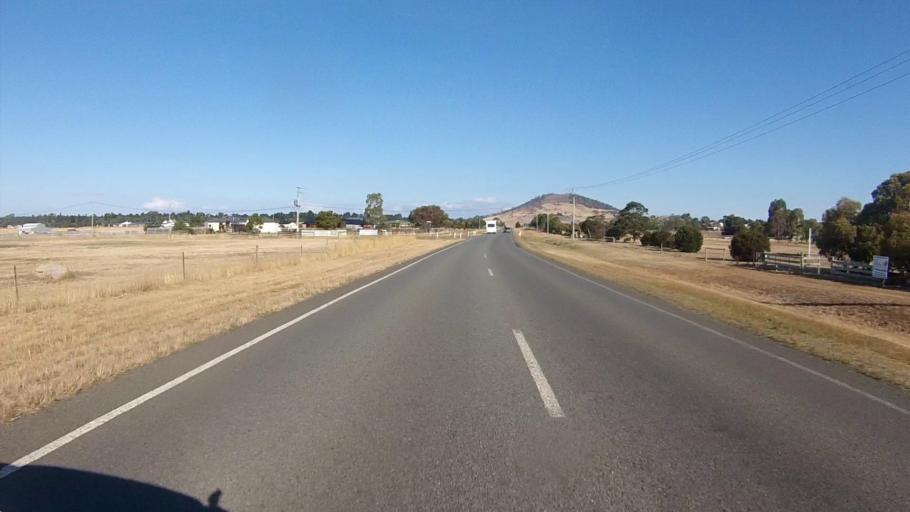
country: AU
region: Tasmania
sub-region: Clarence
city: Seven Mile Beach
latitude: -42.8482
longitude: 147.4822
